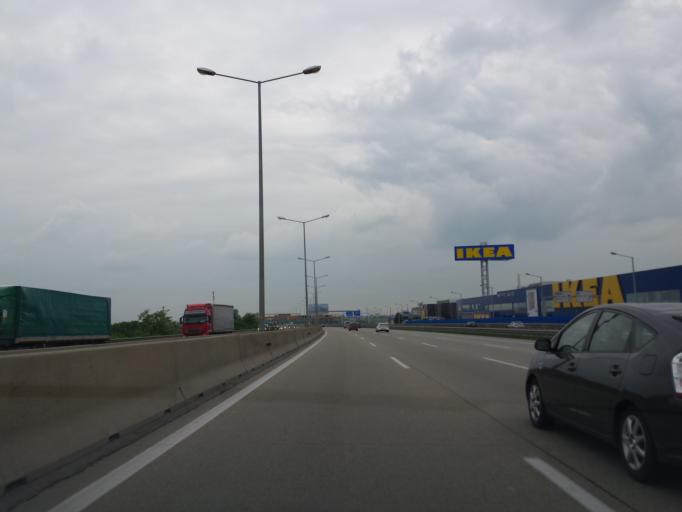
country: AT
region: Lower Austria
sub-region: Politischer Bezirk Modling
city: Wiener Neudorf
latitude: 48.1073
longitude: 16.3170
